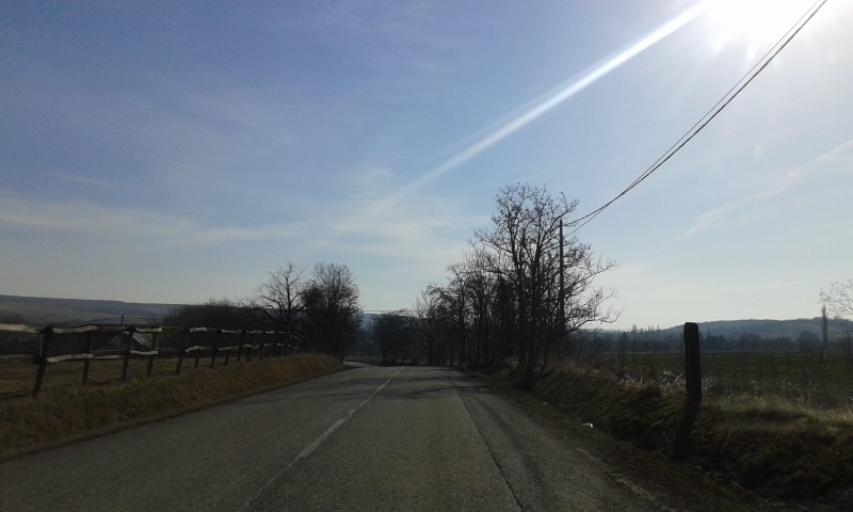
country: HU
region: Pest
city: Soskut
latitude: 47.4073
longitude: 18.8120
